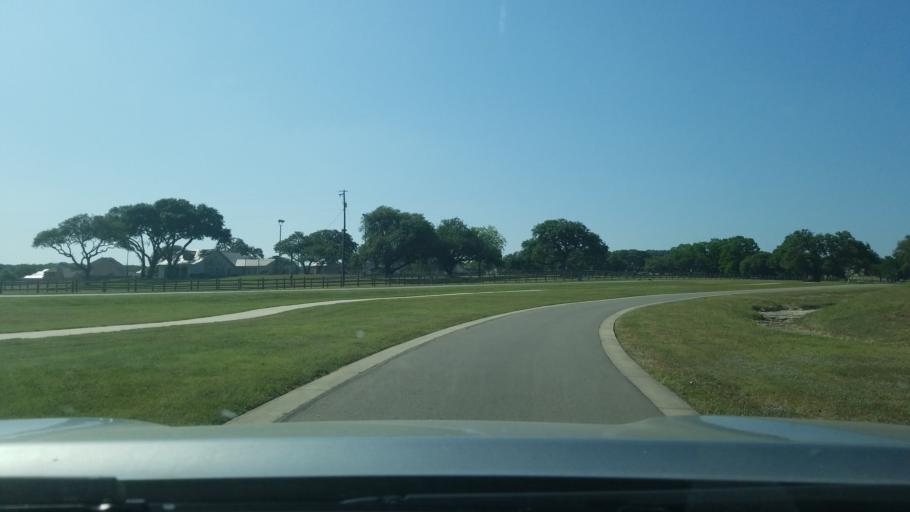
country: US
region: Texas
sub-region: Comal County
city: Bulverde
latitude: 29.7546
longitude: -98.4183
